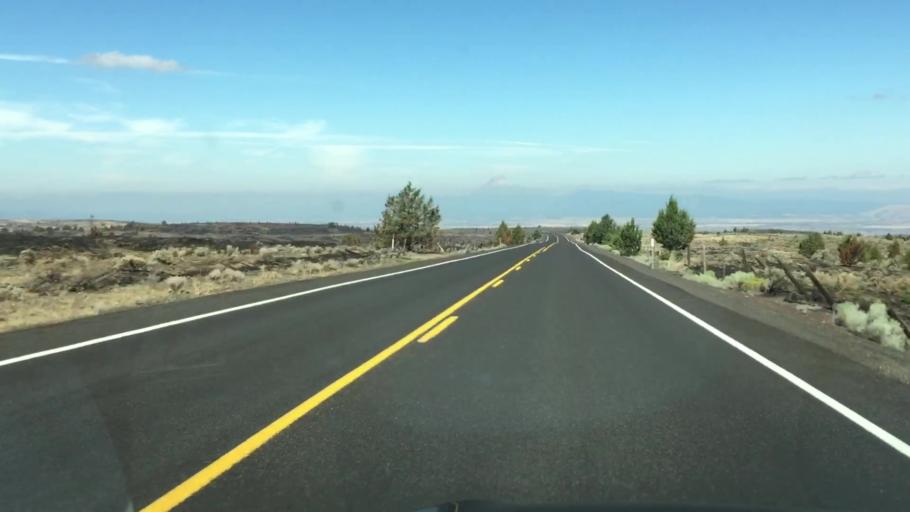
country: US
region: Oregon
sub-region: Jefferson County
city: Warm Springs
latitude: 45.0544
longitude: -121.0192
